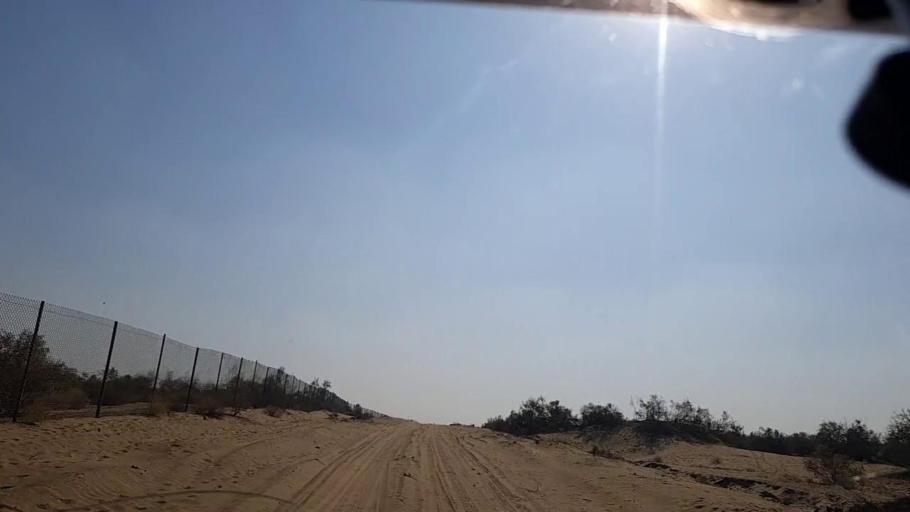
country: PK
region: Sindh
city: Khanpur
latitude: 27.5626
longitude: 69.3887
